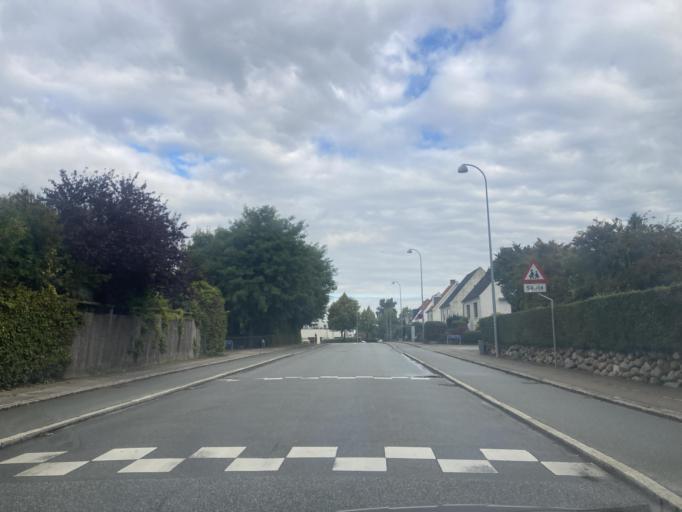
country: DK
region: Capital Region
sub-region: Gladsaxe Municipality
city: Buddinge
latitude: 55.7540
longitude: 12.4833
